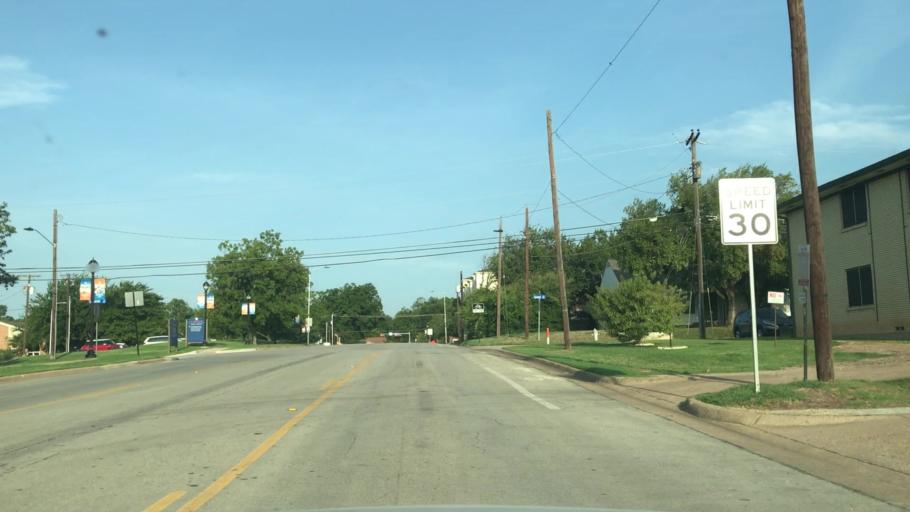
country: US
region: Texas
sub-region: Tarrant County
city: Arlington
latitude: 32.7344
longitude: -97.1211
